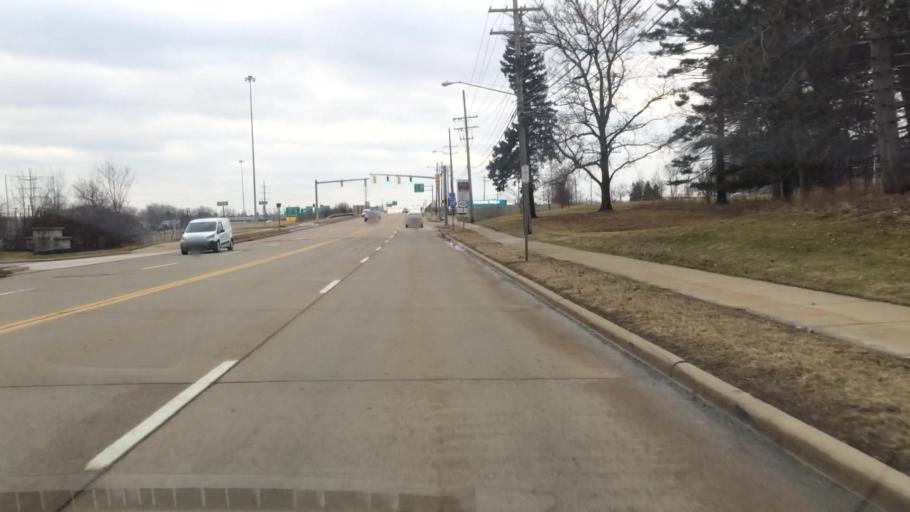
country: US
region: Ohio
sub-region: Cuyahoga County
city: Orange
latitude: 41.4408
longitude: -81.4979
